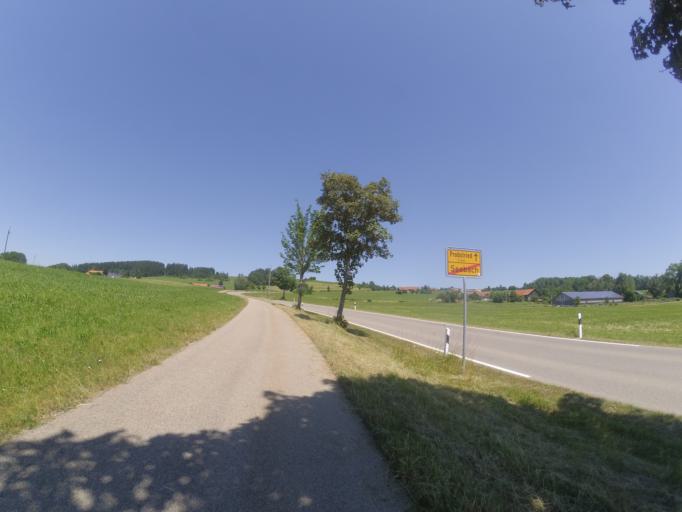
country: DE
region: Bavaria
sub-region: Swabia
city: Haldenwang
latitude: 47.8176
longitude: 10.3436
